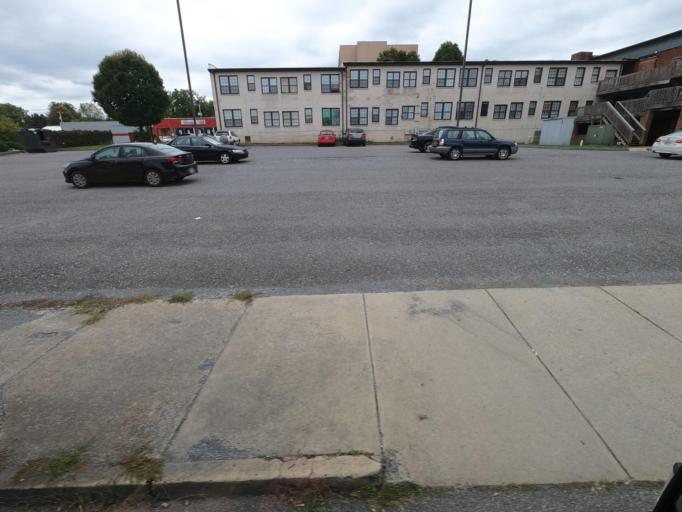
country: US
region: Tennessee
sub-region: Washington County
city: Johnson City
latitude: 36.3171
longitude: -82.3593
